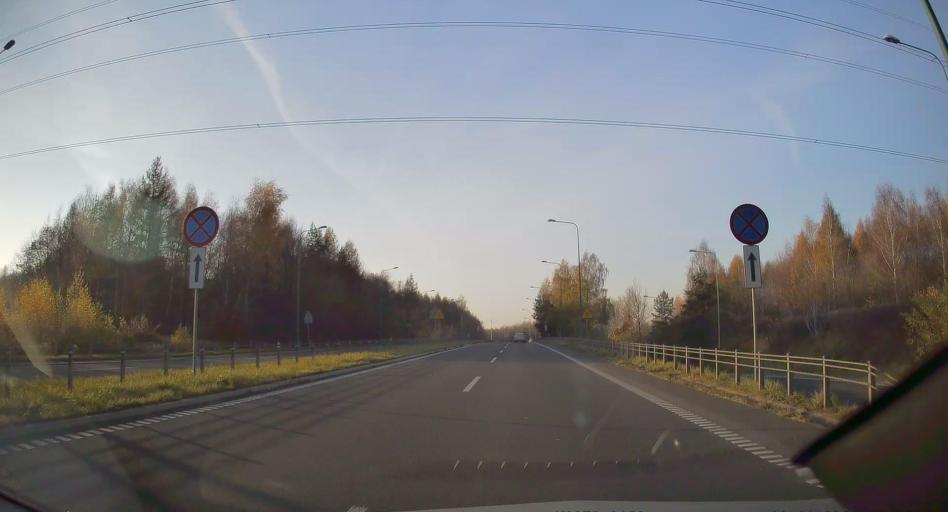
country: PL
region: Silesian Voivodeship
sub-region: Dabrowa Gornicza
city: Dabrowa Gornicza
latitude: 50.3163
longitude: 19.3059
